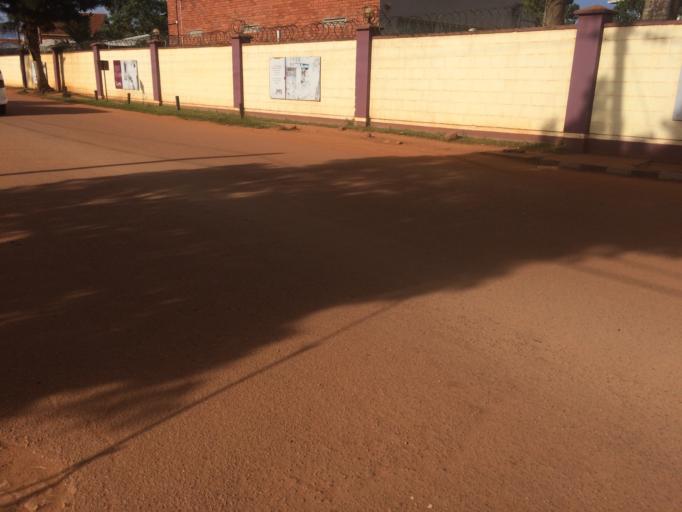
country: UG
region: Central Region
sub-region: Kampala District
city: Kampala
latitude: 0.2962
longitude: 32.5955
